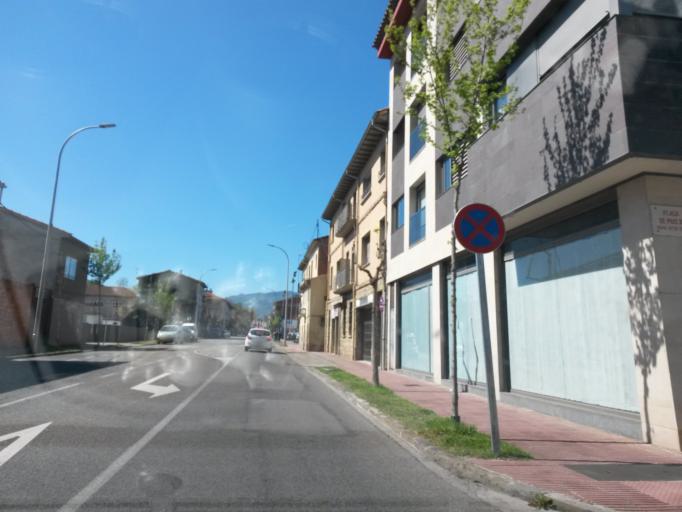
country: ES
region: Catalonia
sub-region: Provincia de Girona
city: Olot
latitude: 42.1710
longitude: 2.4776
